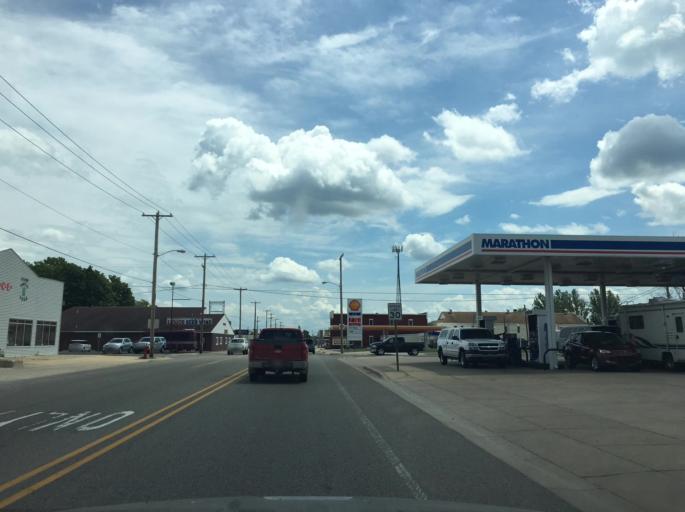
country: US
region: Michigan
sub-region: Crawford County
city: Grayling
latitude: 44.6635
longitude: -84.7177
